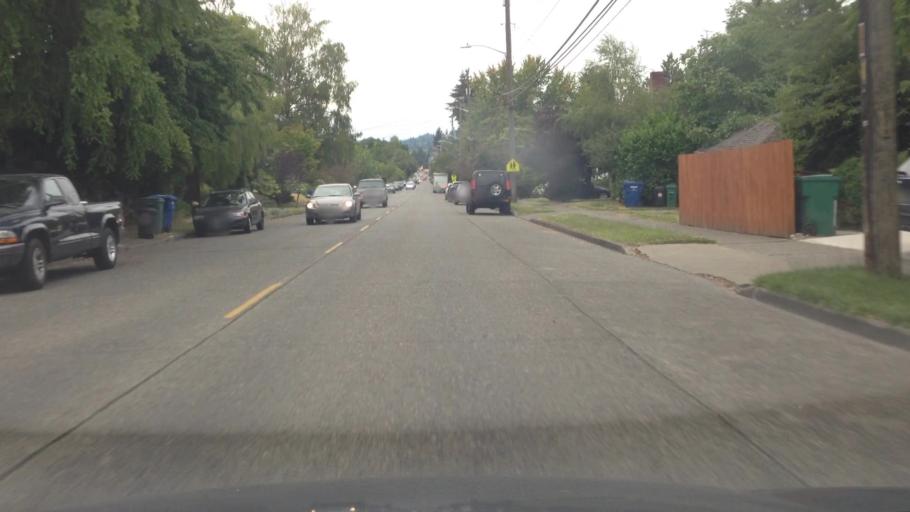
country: US
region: Washington
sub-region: King County
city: Inglewood-Finn Hill
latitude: 47.6735
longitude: -122.2849
